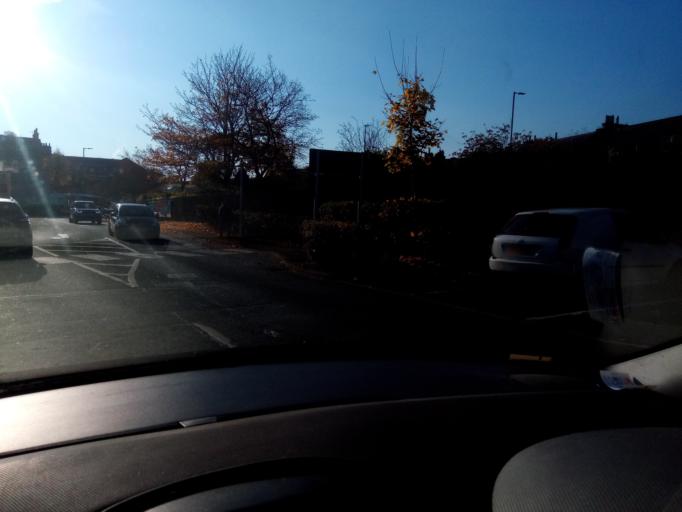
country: GB
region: Scotland
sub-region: The Scottish Borders
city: Hawick
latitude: 55.4269
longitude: -2.7827
